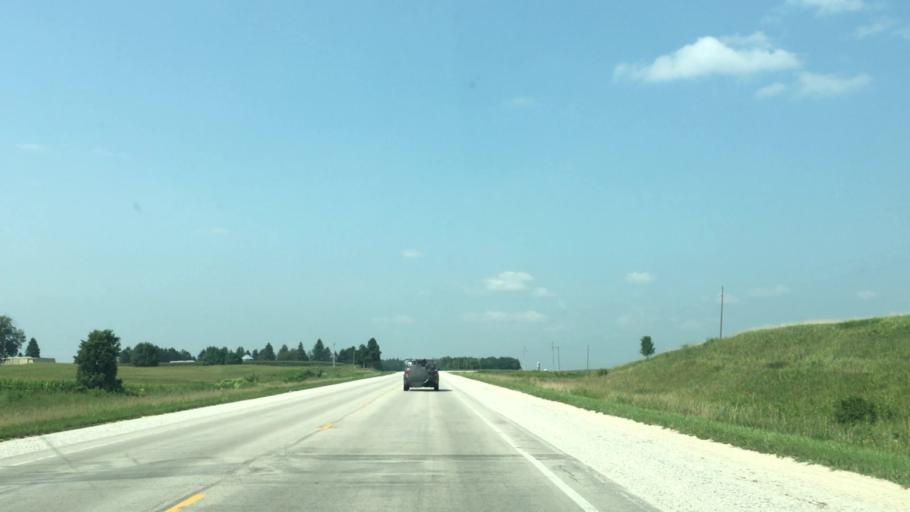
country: US
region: Minnesota
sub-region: Fillmore County
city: Harmony
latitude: 43.4837
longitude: -91.8704
